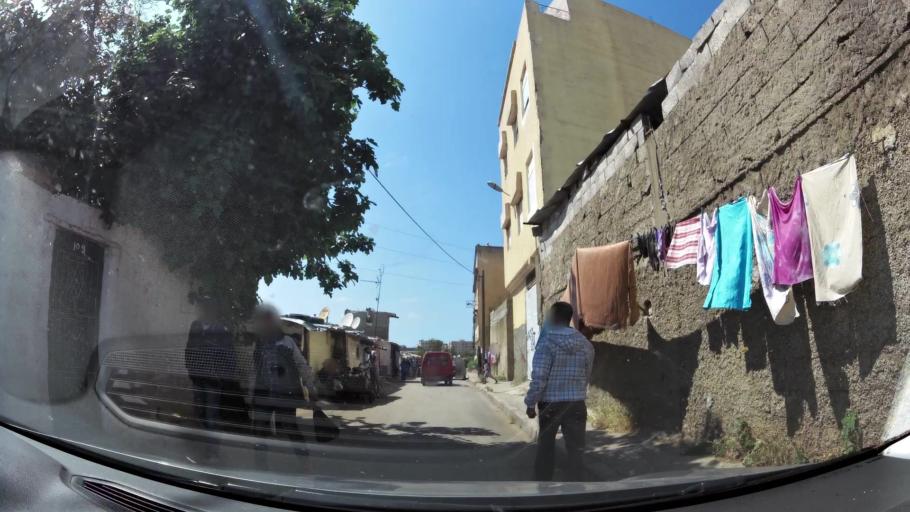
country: MA
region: Rabat-Sale-Zemmour-Zaer
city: Sale
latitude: 34.0358
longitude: -6.7988
